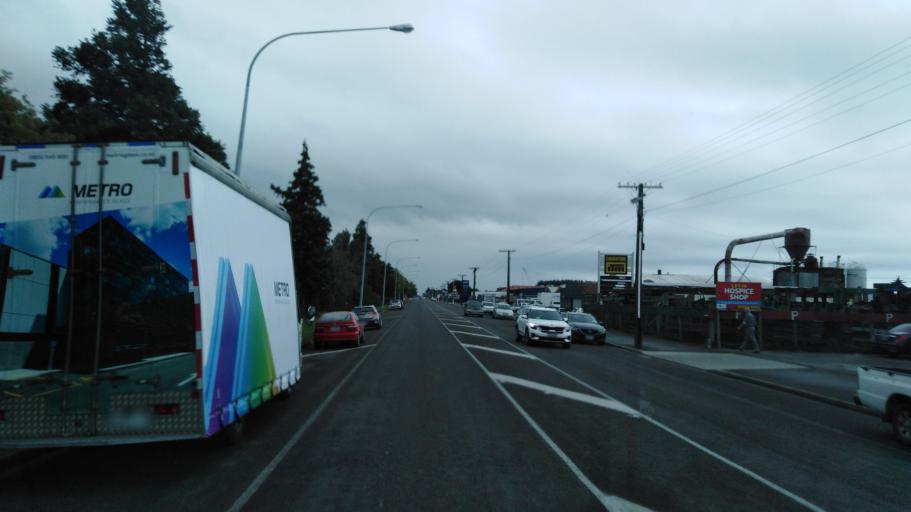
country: NZ
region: Manawatu-Wanganui
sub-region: Horowhenua District
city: Levin
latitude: -40.6337
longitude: 175.2752
